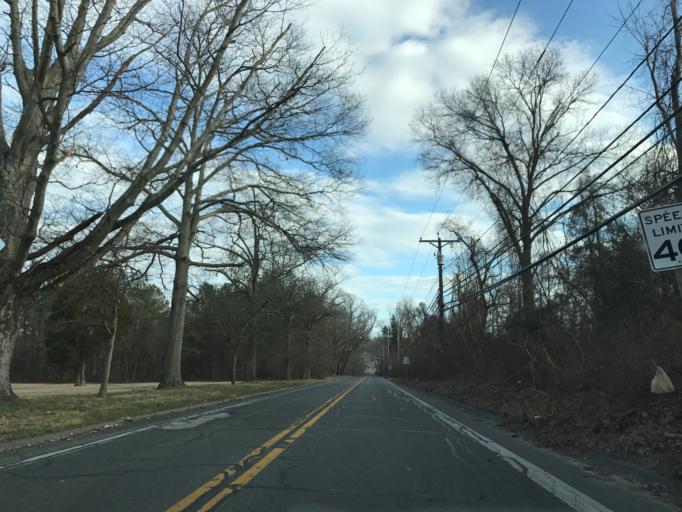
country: US
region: Maryland
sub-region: Anne Arundel County
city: Gambrills
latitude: 39.0586
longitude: -76.6267
